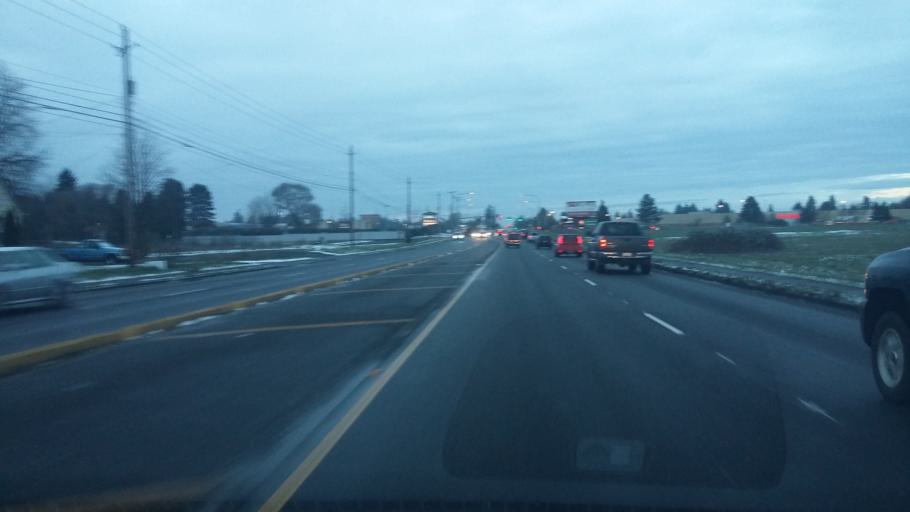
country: US
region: Washington
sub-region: Clark County
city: Orchards
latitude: 45.6720
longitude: -122.5526
